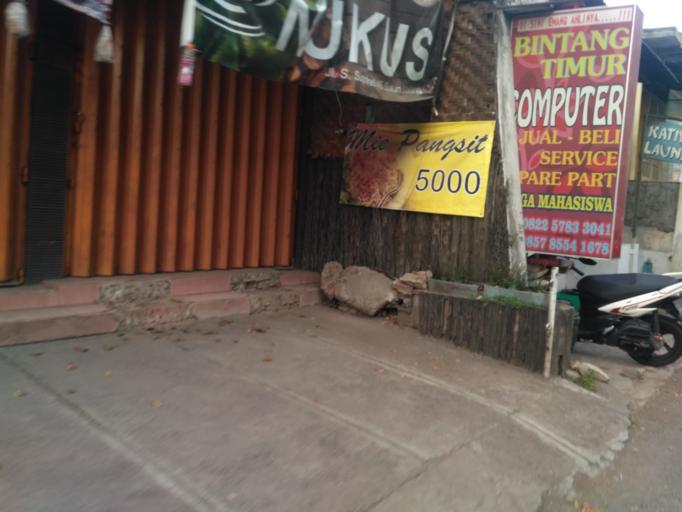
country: ID
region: East Java
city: Kepuh
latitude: -8.0053
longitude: 112.6182
